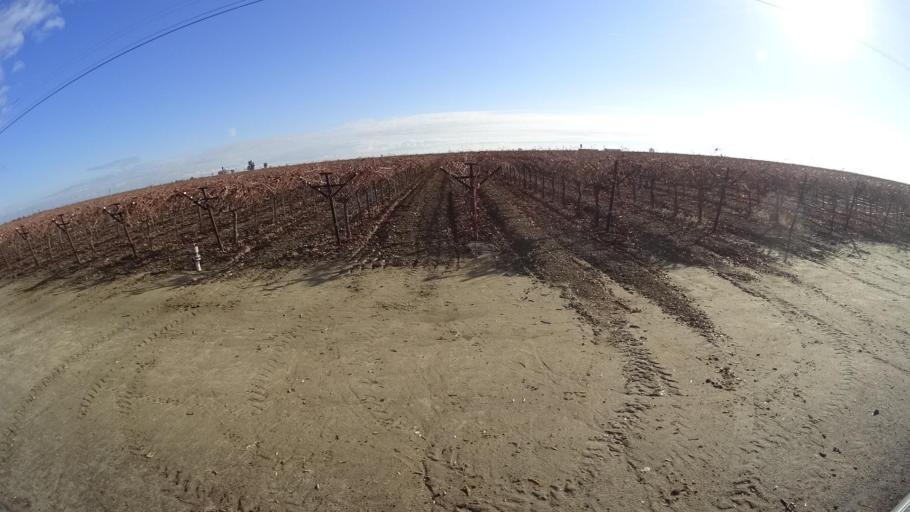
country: US
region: California
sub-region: Kern County
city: Delano
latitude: 35.7213
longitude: -119.3030
